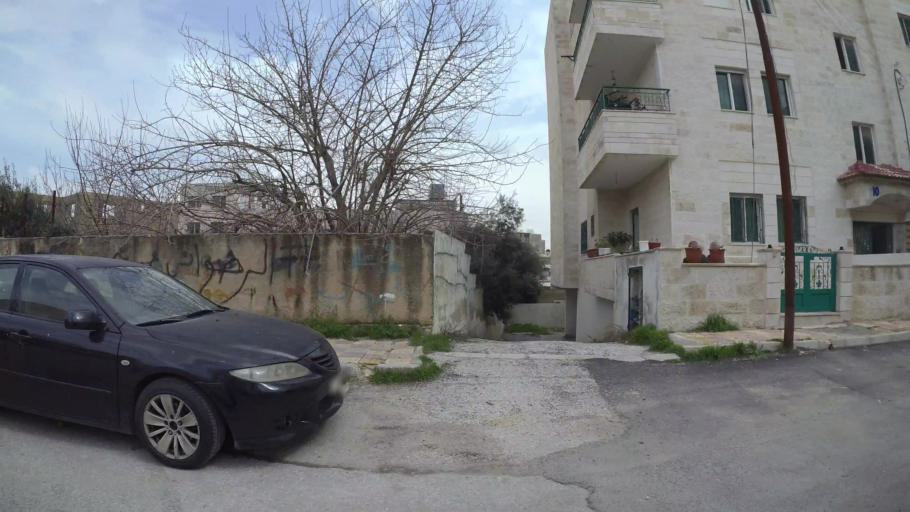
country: JO
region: Amman
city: Umm as Summaq
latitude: 31.8970
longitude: 35.8393
